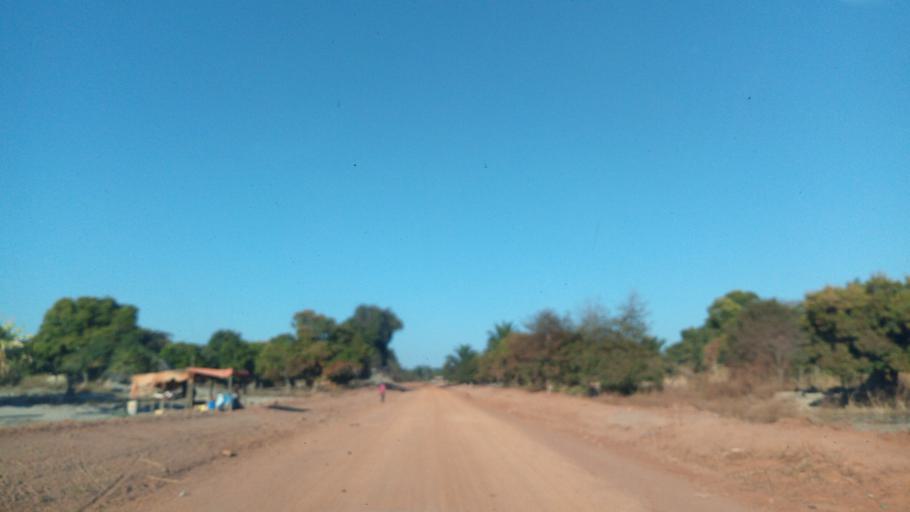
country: ZM
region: Luapula
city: Mwense
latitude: -10.4681
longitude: 28.5185
